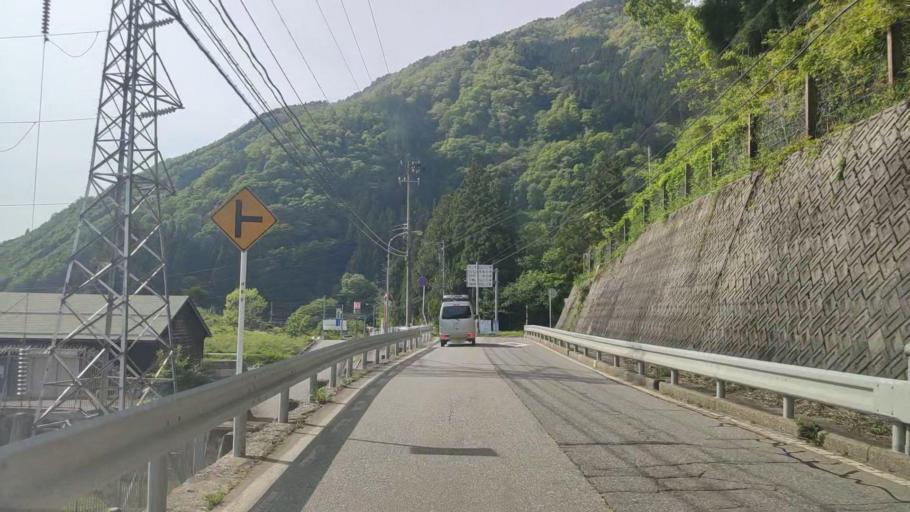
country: JP
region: Gifu
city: Takayama
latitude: 36.2948
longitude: 137.3709
